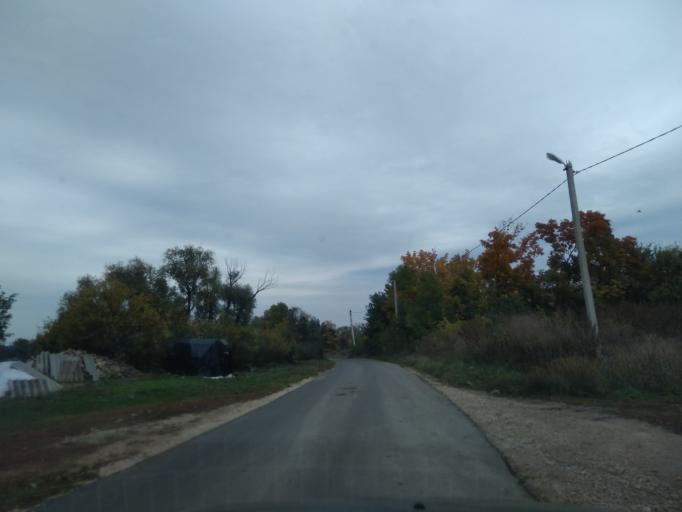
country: RU
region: Lipetsk
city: Zadonsk
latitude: 52.2911
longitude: 38.9456
